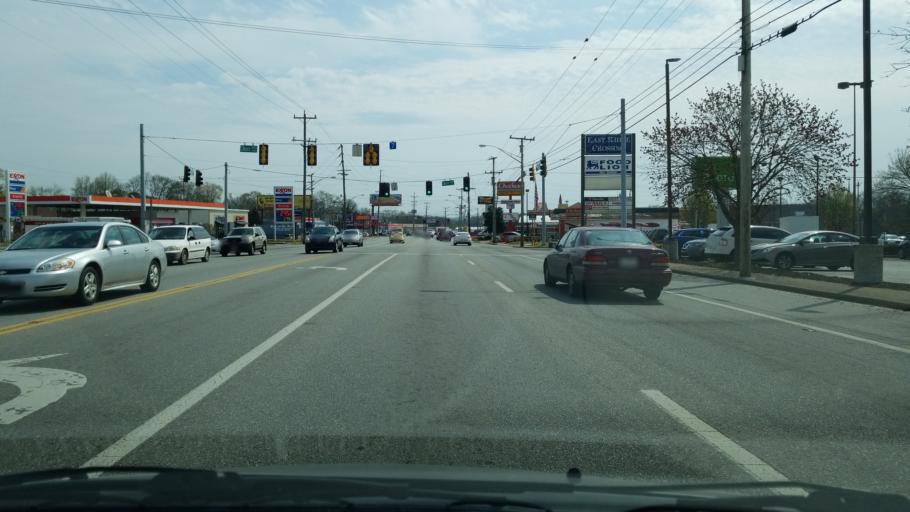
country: US
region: Tennessee
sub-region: Hamilton County
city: East Ridge
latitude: 34.9959
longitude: -85.2381
